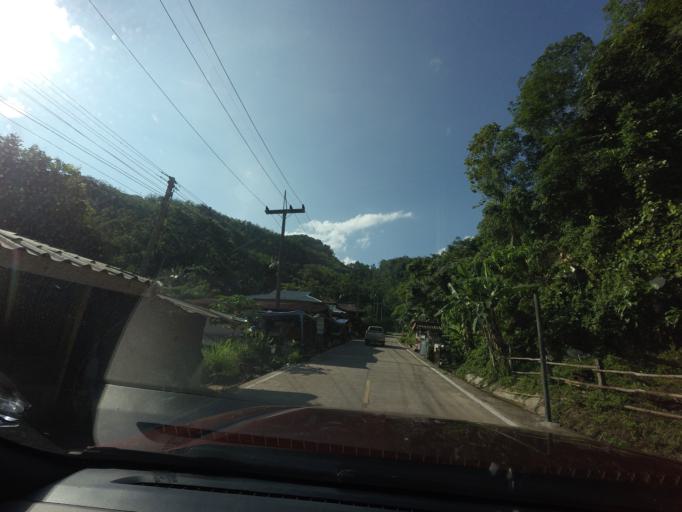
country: TH
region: Yala
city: Than To
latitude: 6.0971
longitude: 101.3123
